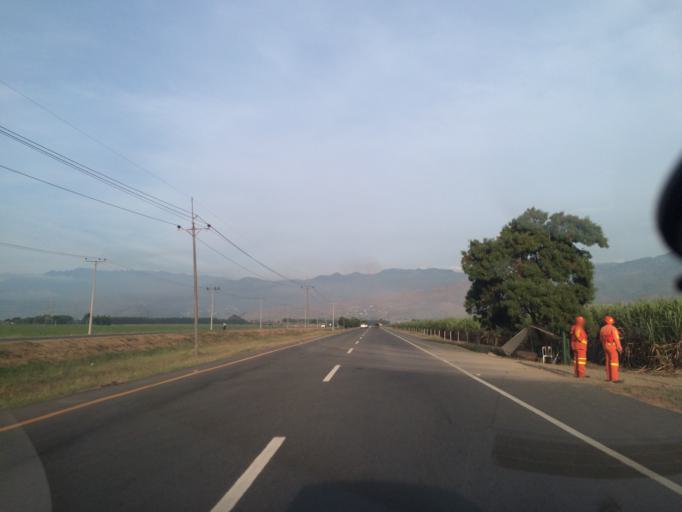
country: CO
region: Valle del Cauca
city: Yumbo
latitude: 3.5544
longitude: -76.4741
